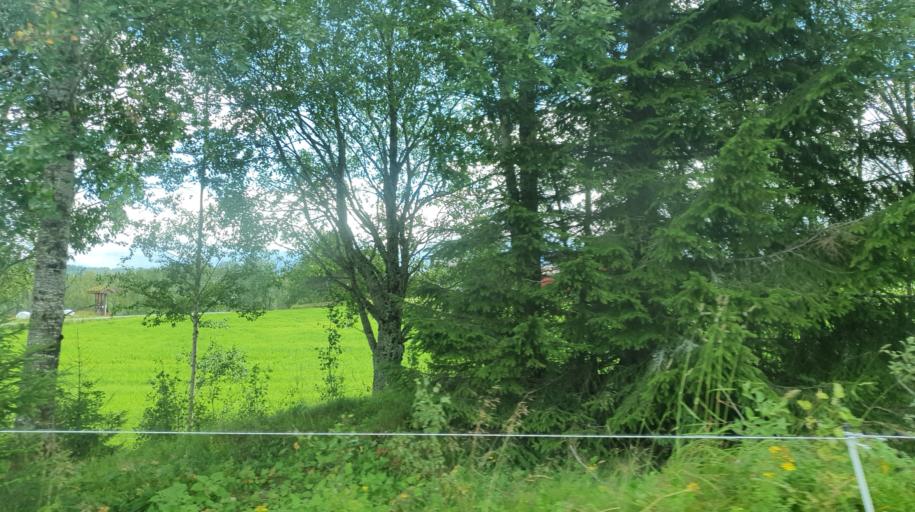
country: NO
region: Nord-Trondelag
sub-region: Levanger
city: Skogn
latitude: 63.5551
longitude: 11.1672
